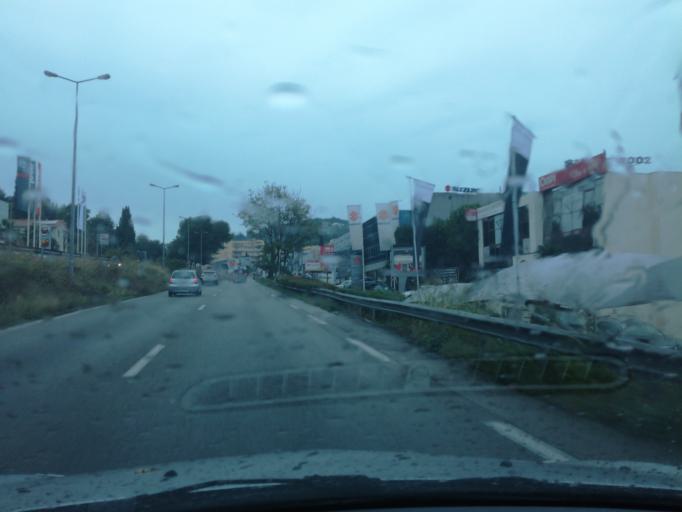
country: FR
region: Provence-Alpes-Cote d'Azur
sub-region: Departement des Alpes-Maritimes
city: Le Cannet
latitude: 43.5761
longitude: 7.0122
